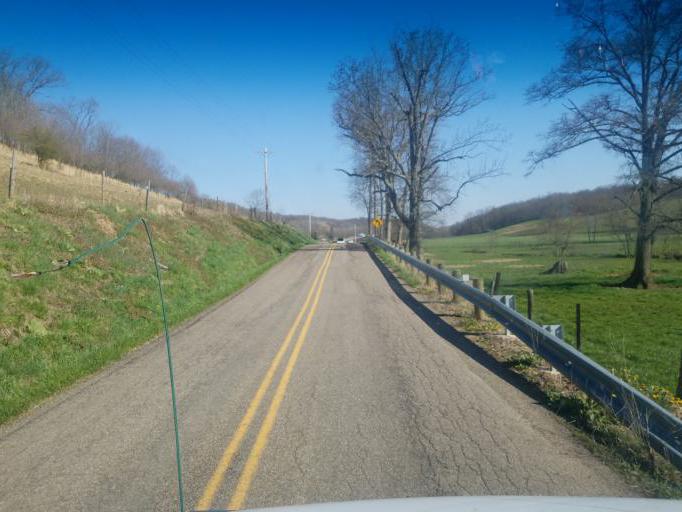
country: US
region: Ohio
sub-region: Muskingum County
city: Frazeysburg
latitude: 40.2470
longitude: -82.2050
